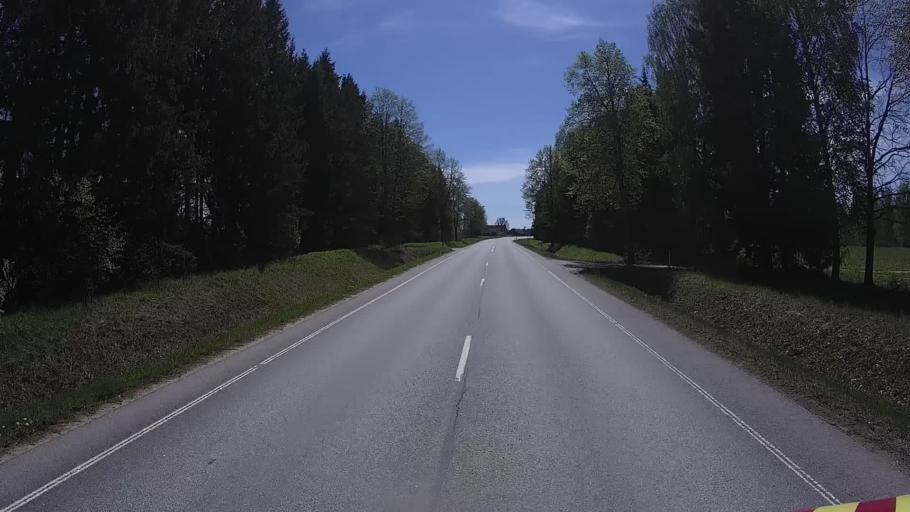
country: EE
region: Vorumaa
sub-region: Voru linn
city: Voru
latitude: 57.8996
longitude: 27.1820
